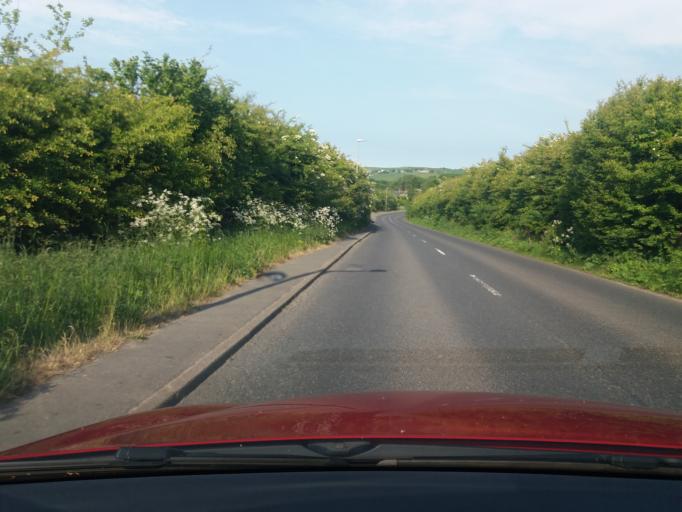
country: GB
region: England
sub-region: Lancashire
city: Chorley
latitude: 53.6924
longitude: -2.5495
